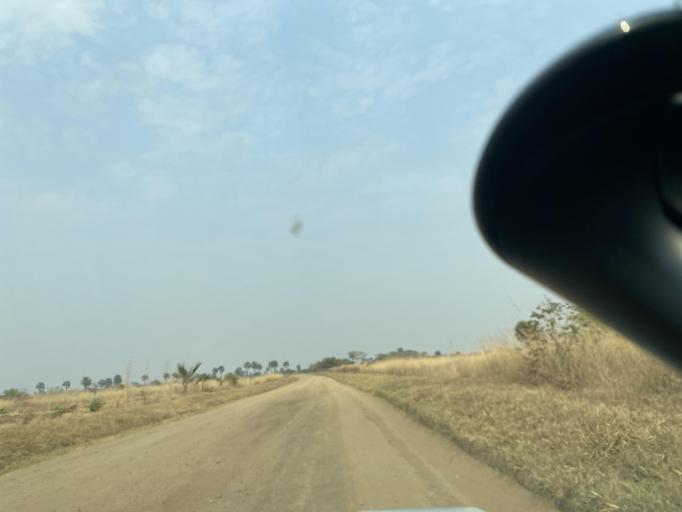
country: ZM
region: Lusaka
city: Kafue
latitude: -15.6487
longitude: 28.0691
